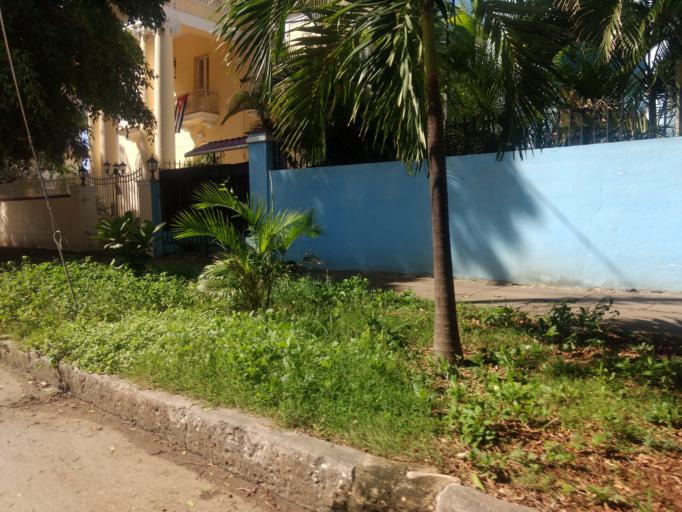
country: CU
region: La Habana
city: Havana
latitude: 23.1329
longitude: -82.3998
